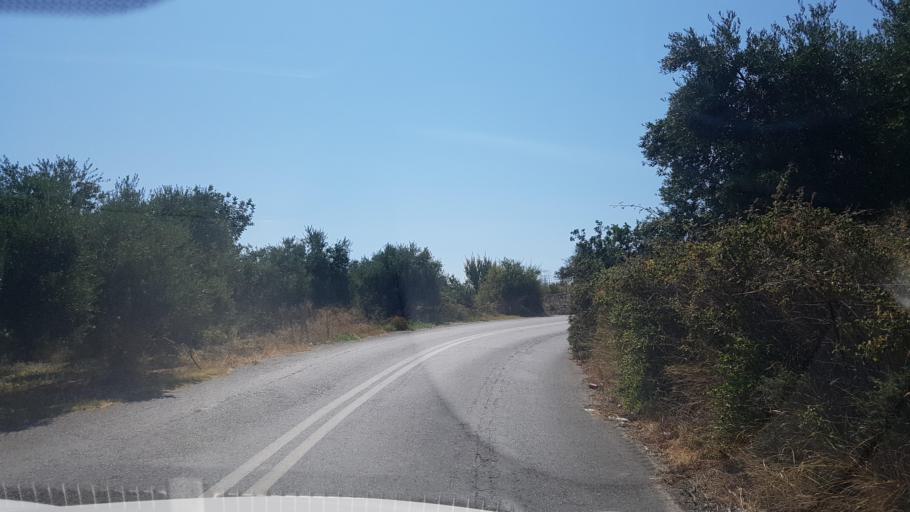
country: GR
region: Crete
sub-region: Nomos Rethymnis
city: Panormos
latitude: 35.3751
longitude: 24.5973
